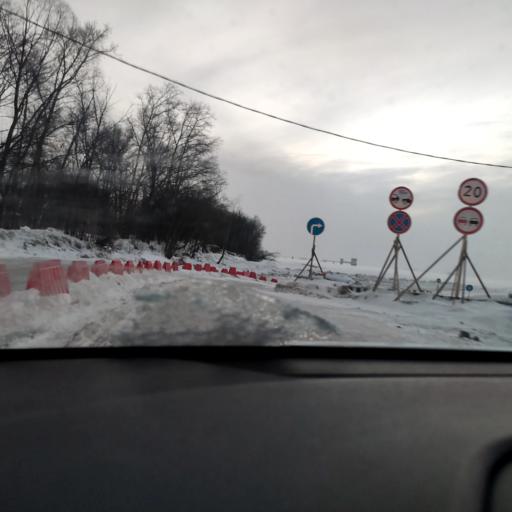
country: RU
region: Tatarstan
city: Staroye Arakchino
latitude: 55.7992
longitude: 48.9779
